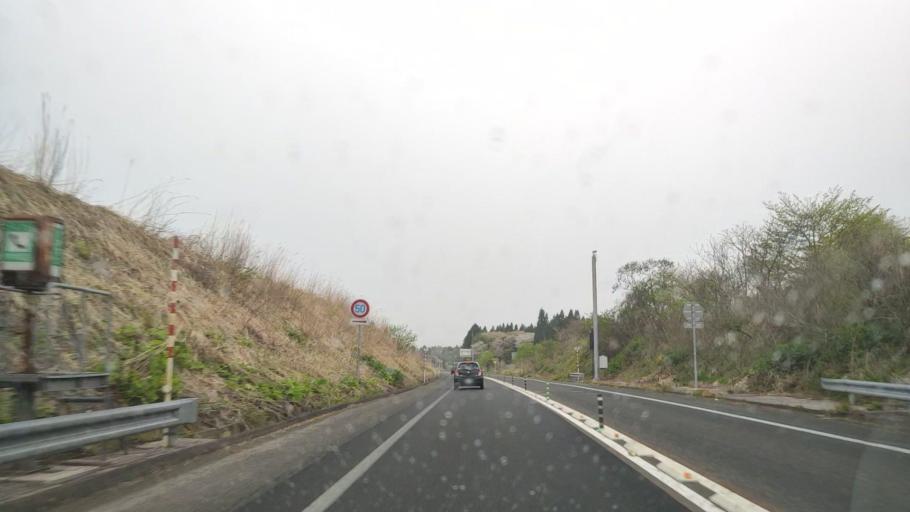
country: JP
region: Akita
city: Noshiromachi
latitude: 40.2081
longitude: 140.1896
